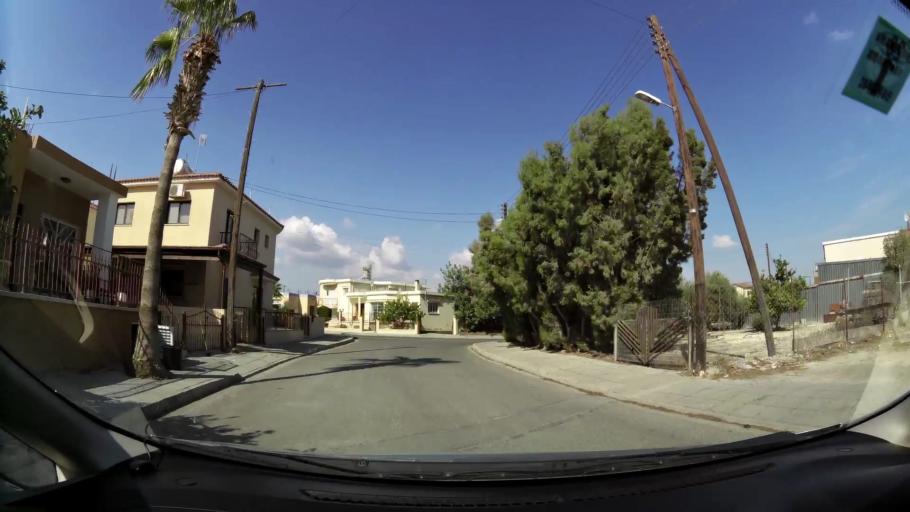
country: CY
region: Larnaka
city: Aradippou
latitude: 34.9503
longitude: 33.5798
